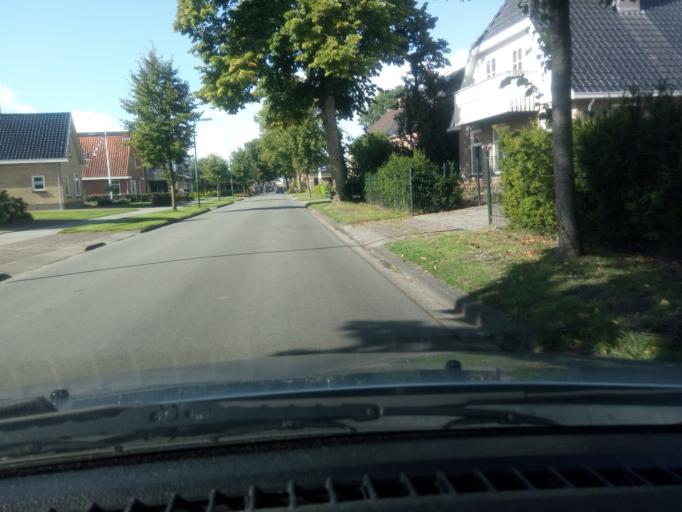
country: NL
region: Friesland
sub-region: Gemeente Achtkarspelen
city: Surhuisterveen
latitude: 53.1846
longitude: 6.1728
